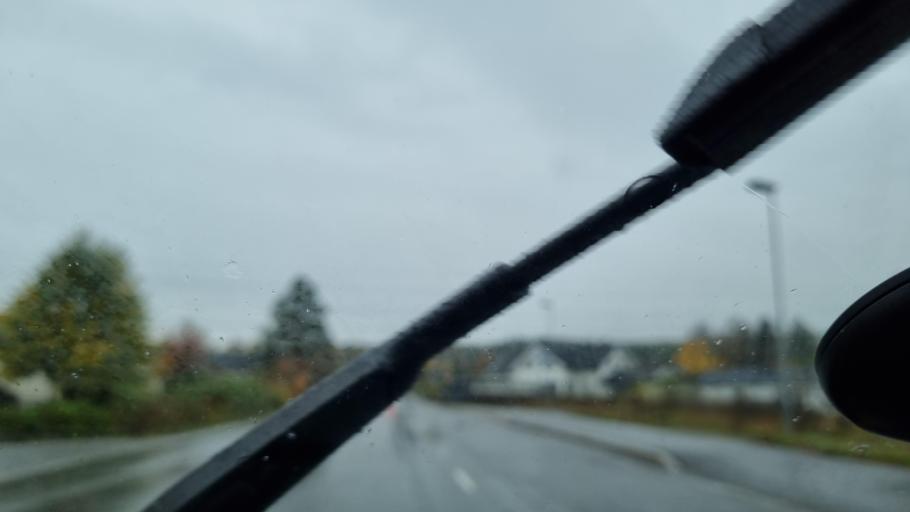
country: NO
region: Hedmark
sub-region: Hamar
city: Hamar
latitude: 60.8264
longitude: 11.0633
